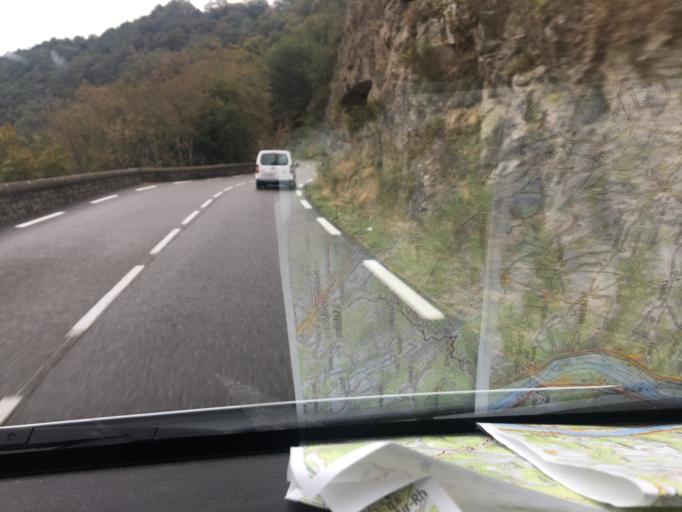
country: FR
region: Rhone-Alpes
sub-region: Departement de l'Ardeche
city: Saint-Jean-de-Muzols
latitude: 45.0561
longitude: 4.7713
